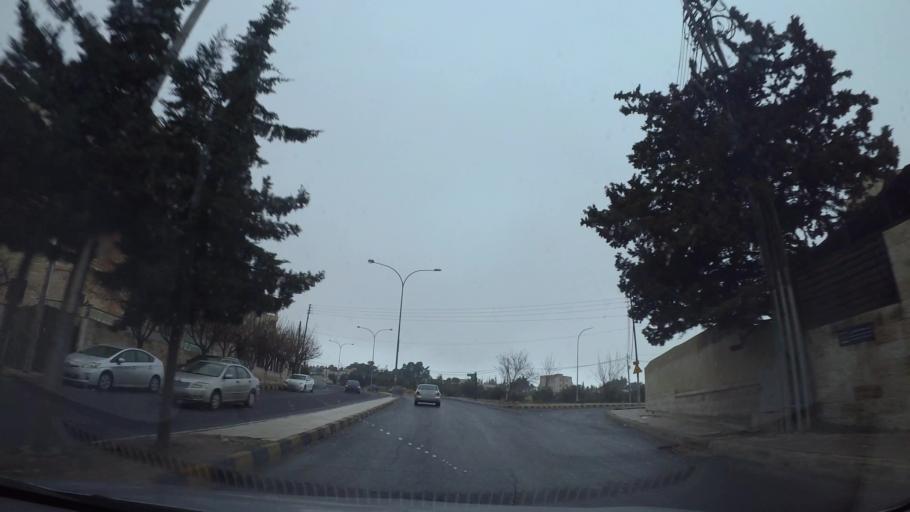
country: JO
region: Amman
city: Al Jubayhah
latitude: 32.0365
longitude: 35.8669
